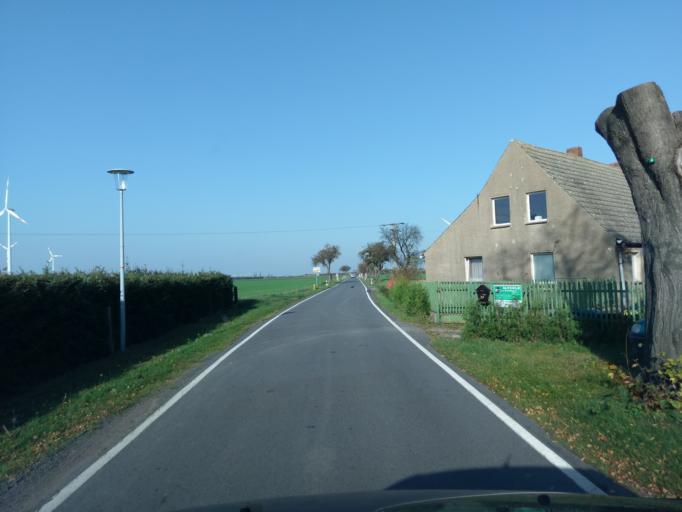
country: DE
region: Brandenburg
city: Muhlberg
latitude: 51.4615
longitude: 13.2577
